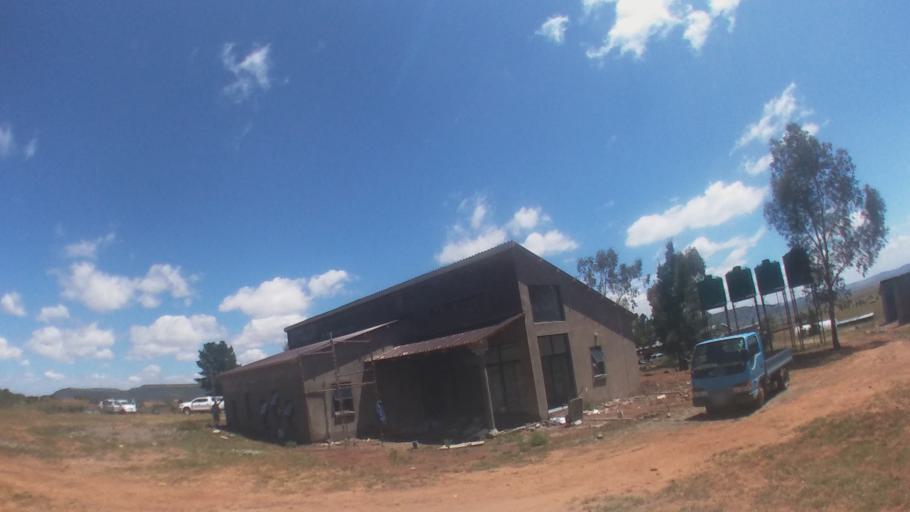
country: LS
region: Maseru
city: Maseru
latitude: -29.4398
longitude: 27.4131
